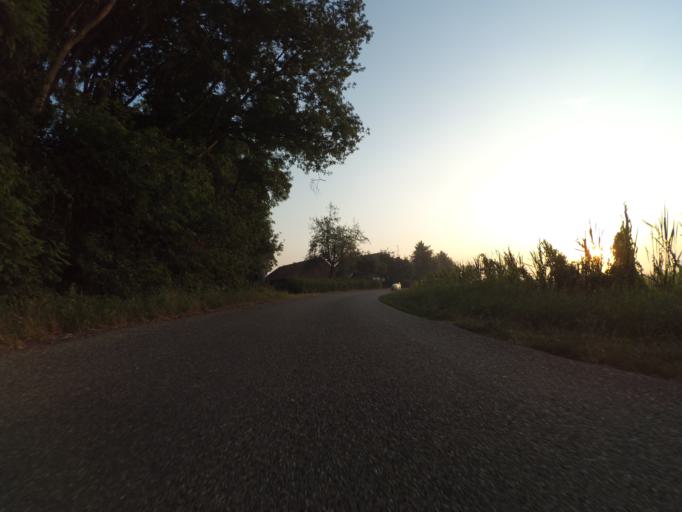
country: NL
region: Overijssel
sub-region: Gemeente Tubbergen
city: Tubbergen
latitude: 52.3998
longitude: 6.8174
